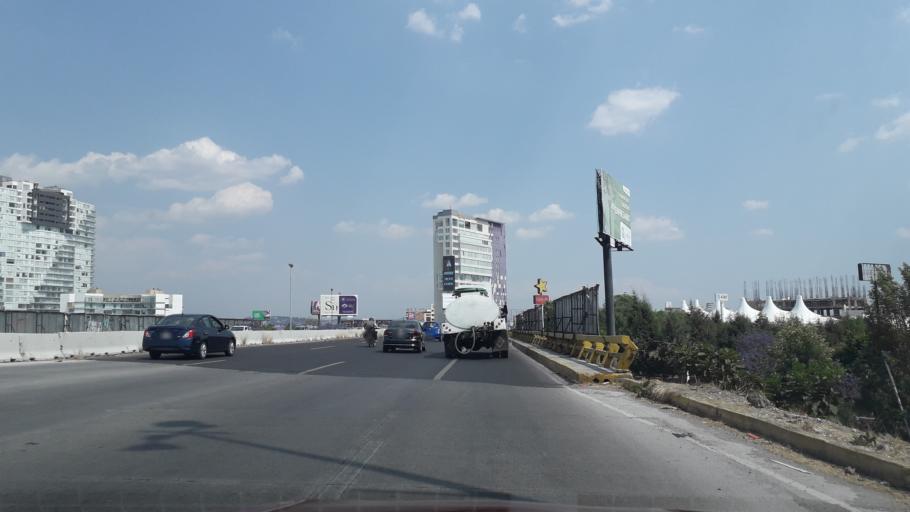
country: MX
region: Puebla
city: Puebla
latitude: 19.0290
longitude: -98.2331
